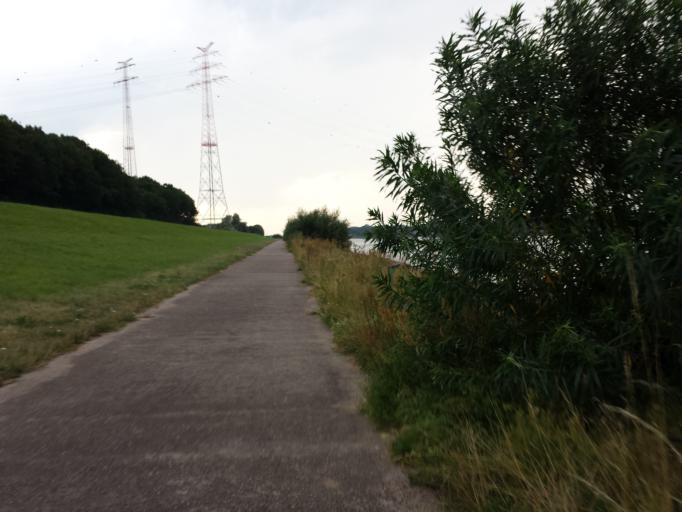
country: DE
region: Lower Saxony
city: Lemwerder
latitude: 53.1223
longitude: 8.6754
